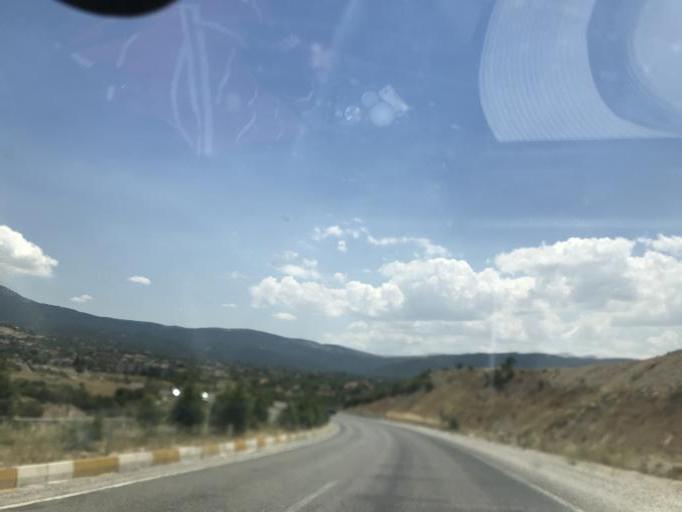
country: TR
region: Denizli
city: Honaz
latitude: 37.7000
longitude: 29.2002
